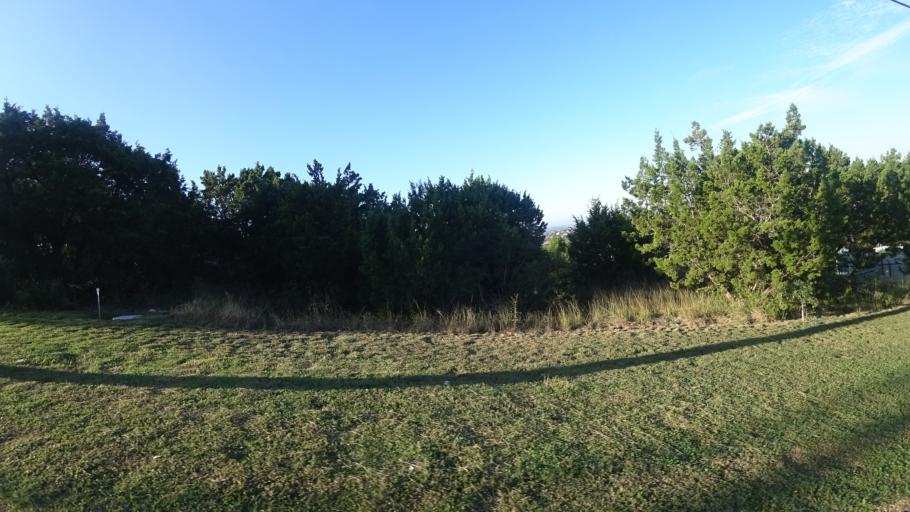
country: US
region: Texas
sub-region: Travis County
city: Hudson Bend
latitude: 30.3699
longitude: -97.8873
